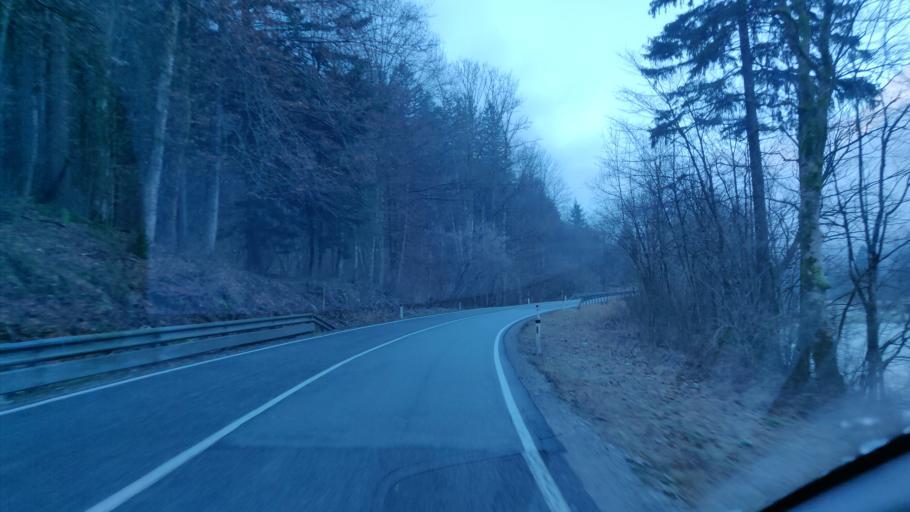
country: SI
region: Gorje
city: Zgornje Gorje
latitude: 46.3042
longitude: 14.0585
